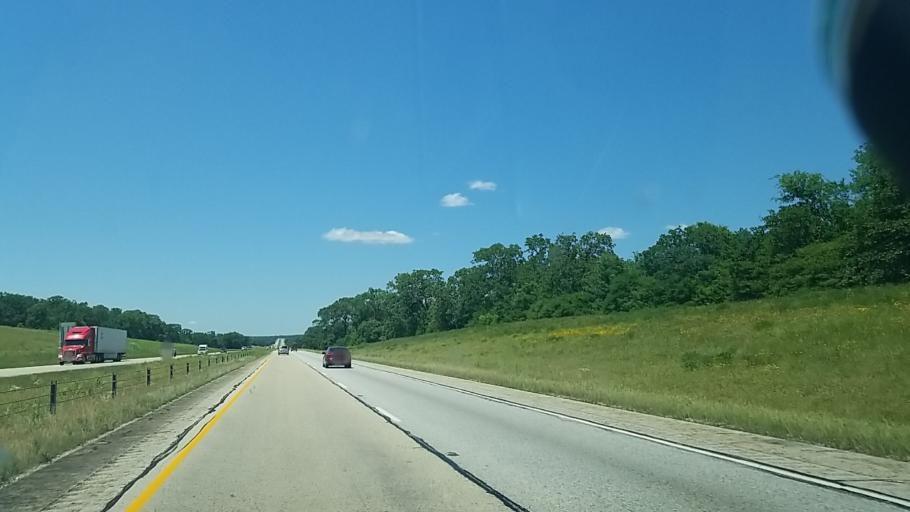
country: US
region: Texas
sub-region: Leon County
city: Centerville
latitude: 31.1667
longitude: -95.9869
